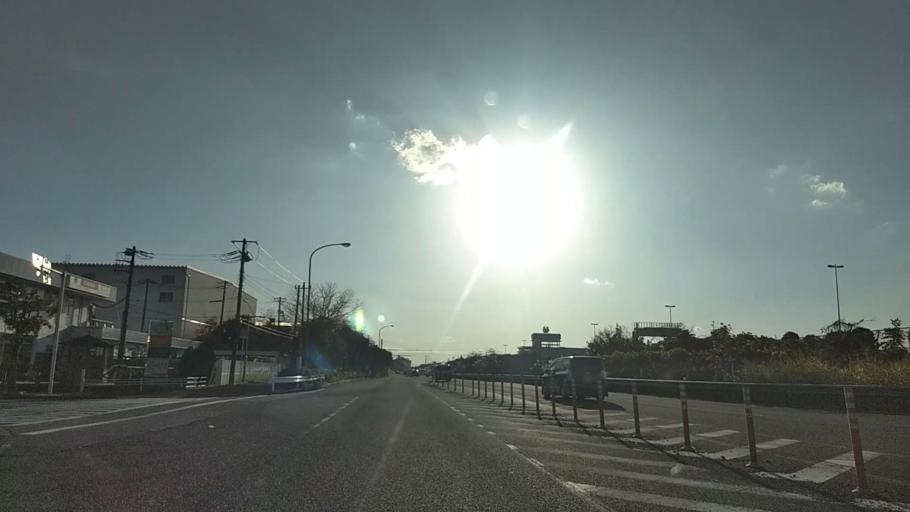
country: JP
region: Tokyo
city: Urayasu
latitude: 35.6670
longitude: 139.9222
